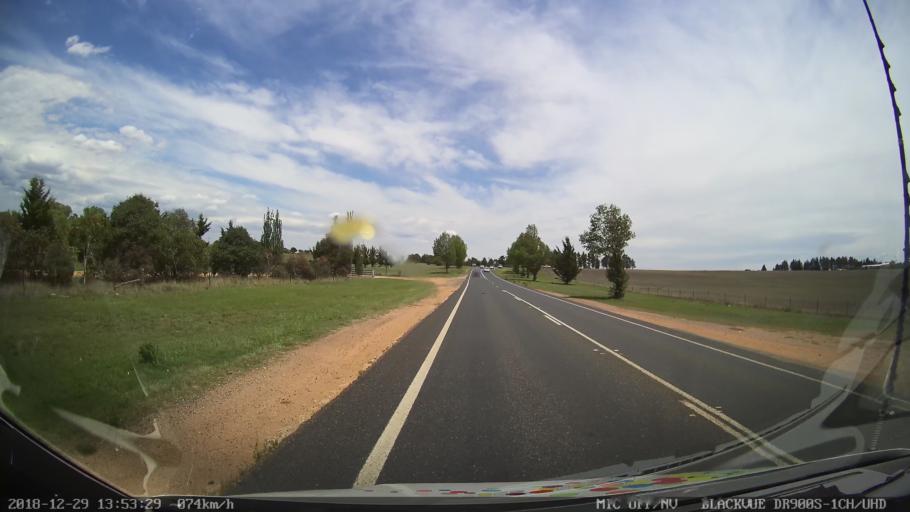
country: AU
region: New South Wales
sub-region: Cooma-Monaro
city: Cooma
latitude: -36.2068
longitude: 149.1574
